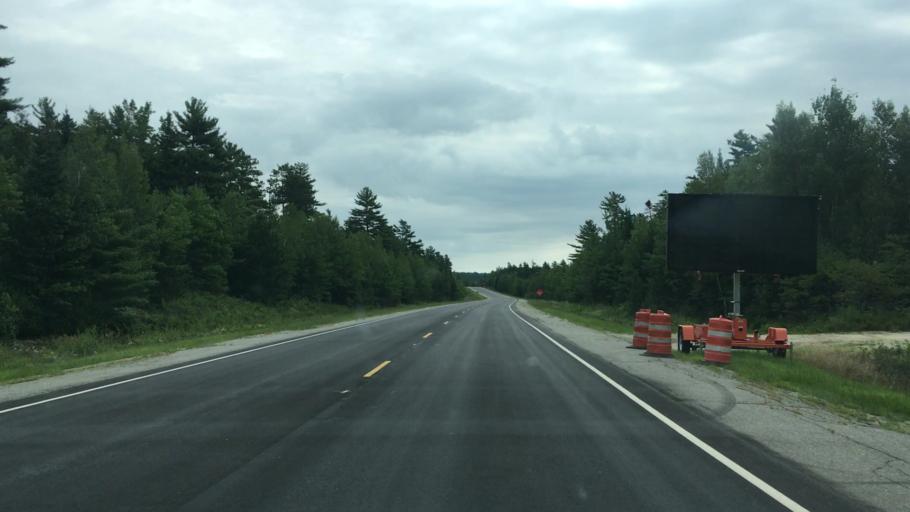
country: US
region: Maine
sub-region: Washington County
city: Addison
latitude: 44.9065
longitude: -67.8261
